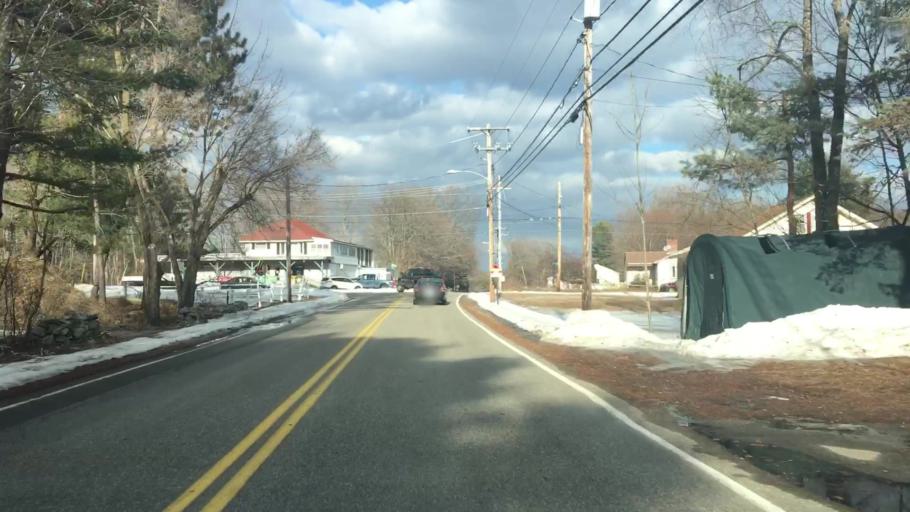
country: US
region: Maine
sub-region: York County
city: Biddeford
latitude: 43.4551
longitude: -70.4300
